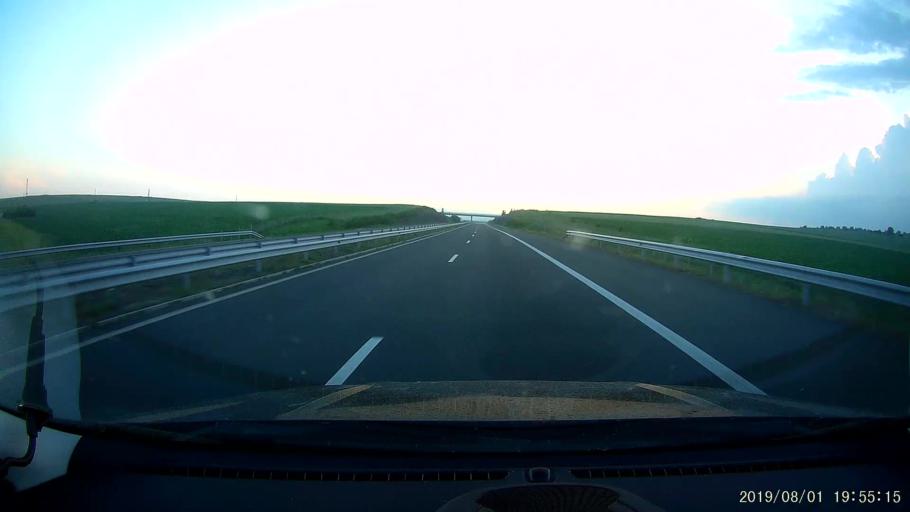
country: BG
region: Burgas
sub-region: Obshtina Karnobat
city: Karnobat
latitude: 42.5700
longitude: 26.8746
